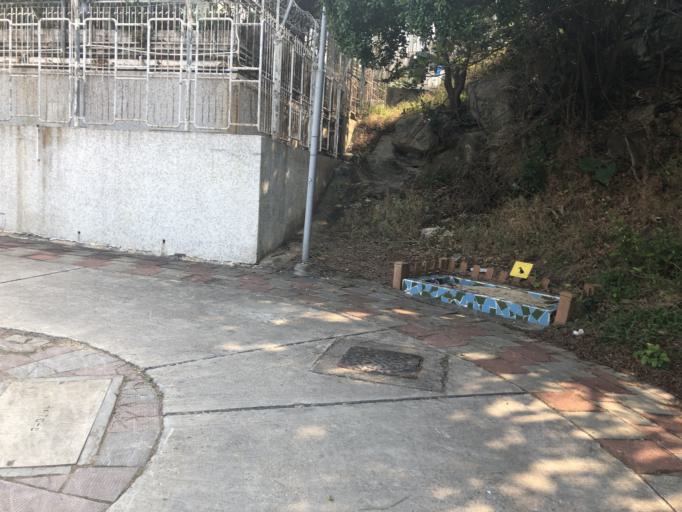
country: HK
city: Yung Shue Wan
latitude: 22.2049
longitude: 114.0237
